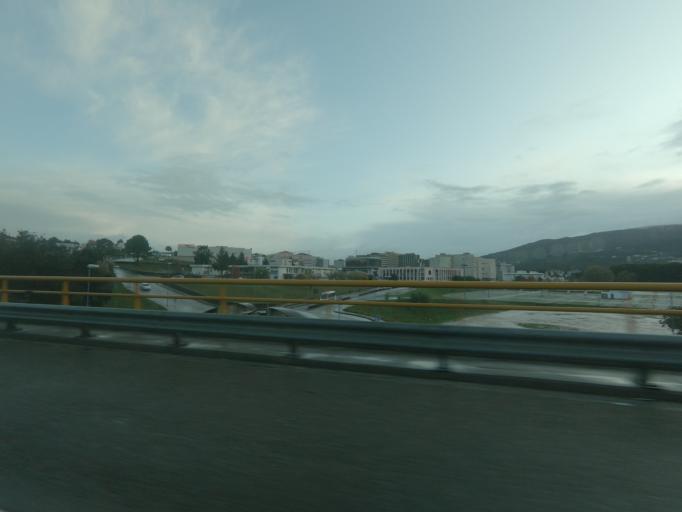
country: PT
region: Viana do Castelo
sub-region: Valenca
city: Valenca
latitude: 42.0218
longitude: -8.6482
